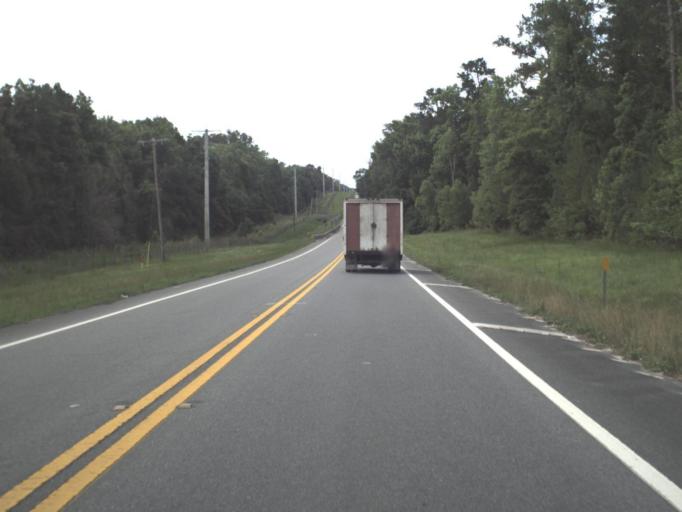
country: US
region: Florida
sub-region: Clay County
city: Asbury Lake
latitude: 29.9407
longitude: -81.8975
